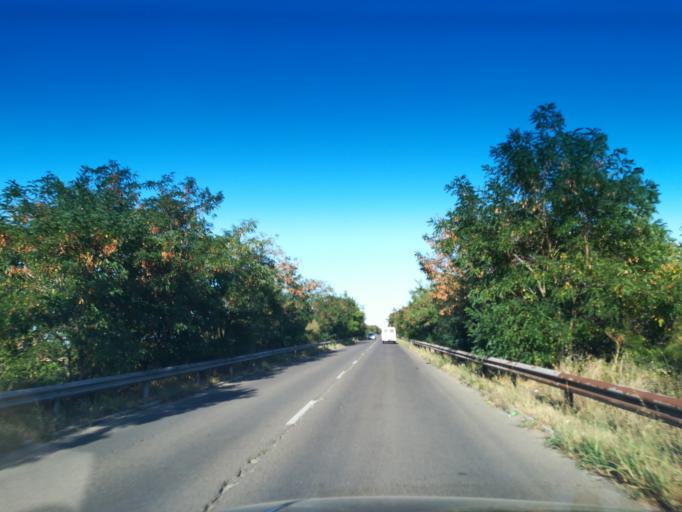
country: BG
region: Stara Zagora
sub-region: Obshtina Chirpan
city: Chirpan
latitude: 42.1718
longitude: 25.1856
